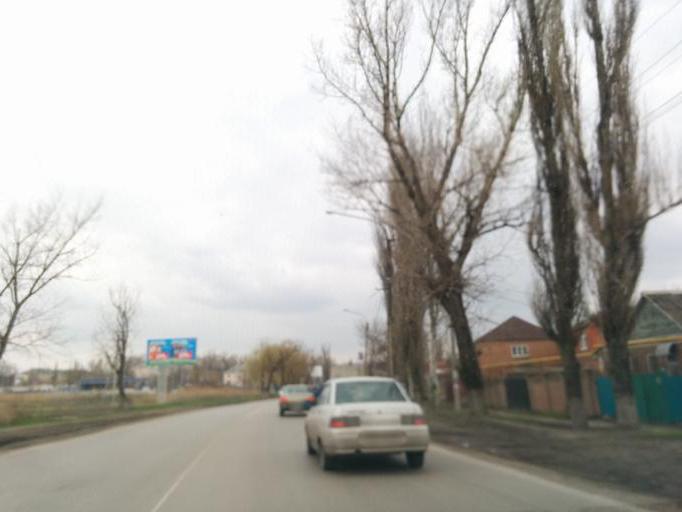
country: RU
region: Rostov
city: Novocherkassk
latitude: 47.4506
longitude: 40.1025
